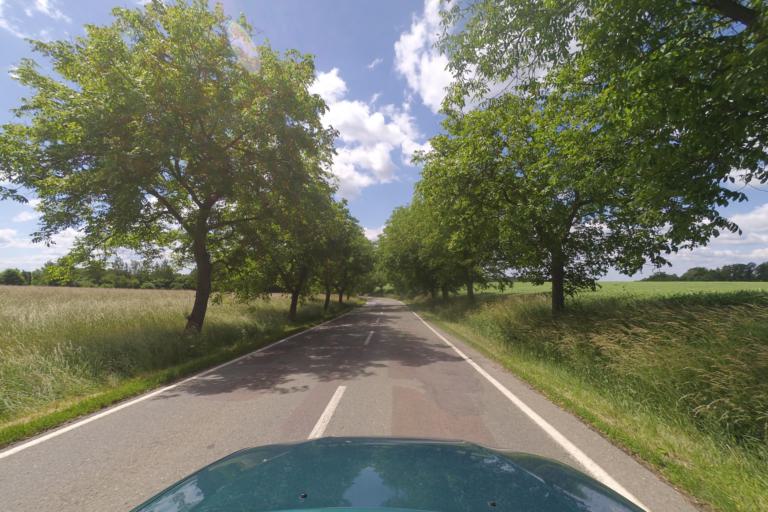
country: CZ
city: Nove Mesto nad Metuji
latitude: 50.3304
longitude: 16.2169
